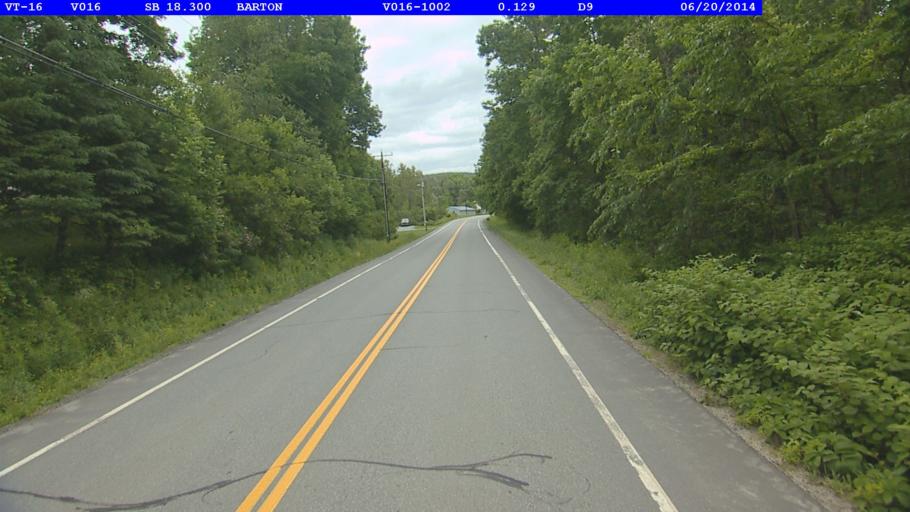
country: US
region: Vermont
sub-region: Orleans County
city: Newport
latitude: 44.7191
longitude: -72.1849
